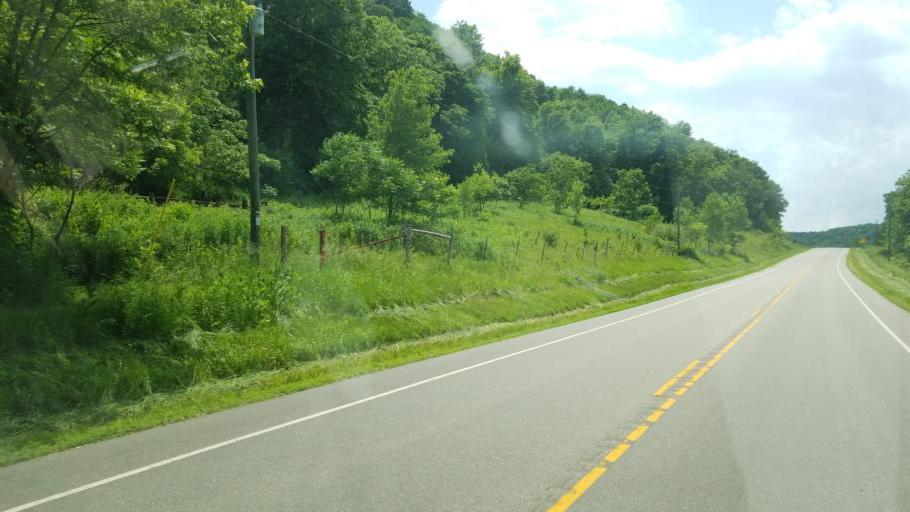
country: US
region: Wisconsin
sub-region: Vernon County
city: Viroqua
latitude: 43.4877
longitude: -90.6857
